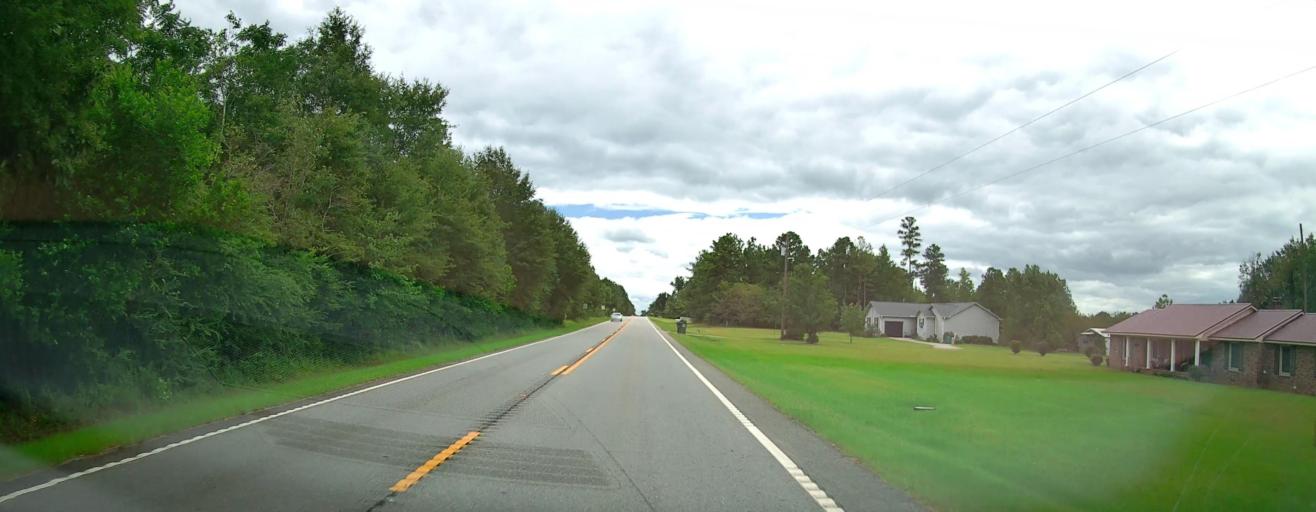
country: US
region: Georgia
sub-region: Twiggs County
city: Jeffersonville
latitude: 32.6730
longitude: -83.3304
